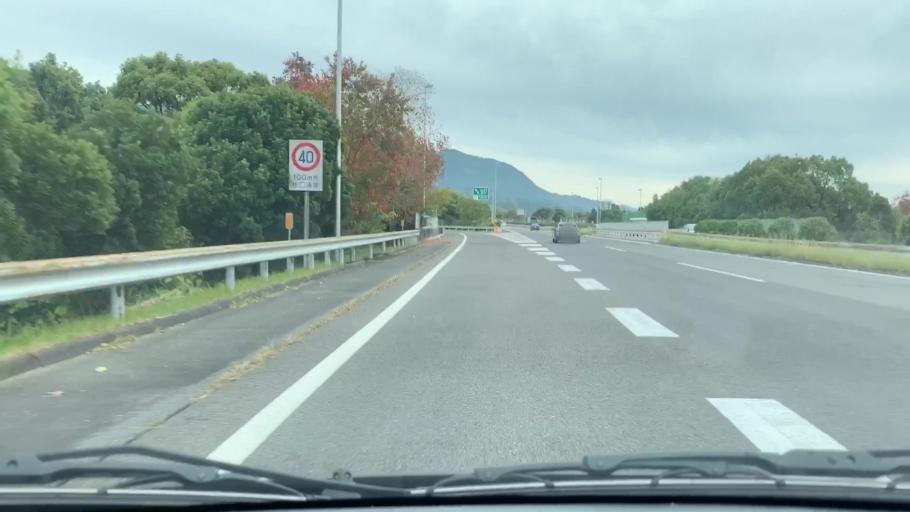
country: JP
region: Saga Prefecture
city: Saga-shi
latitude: 33.3214
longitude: 130.2772
